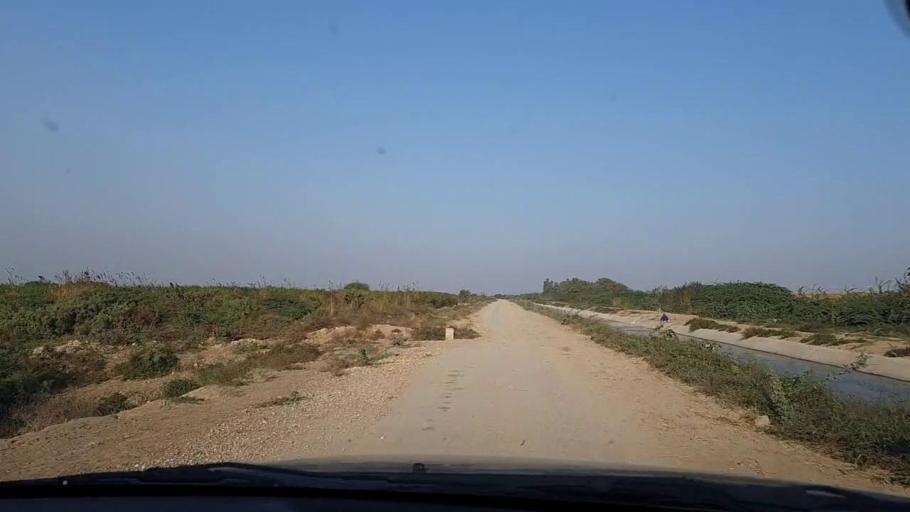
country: PK
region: Sindh
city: Chuhar Jamali
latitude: 24.2865
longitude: 67.7494
